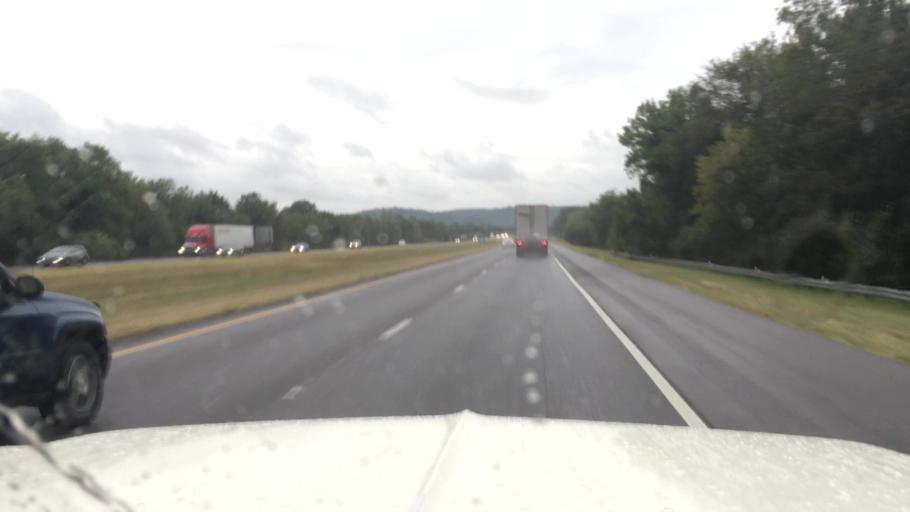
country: US
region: Alabama
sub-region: Morgan County
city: Falkville
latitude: 34.3581
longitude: -86.8918
